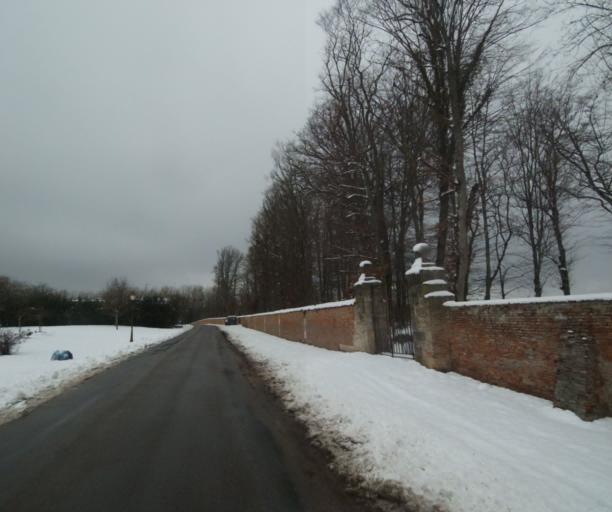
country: FR
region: Champagne-Ardenne
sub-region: Departement de la Haute-Marne
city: Laneuville-a-Remy
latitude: 48.4723
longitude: 4.8809
